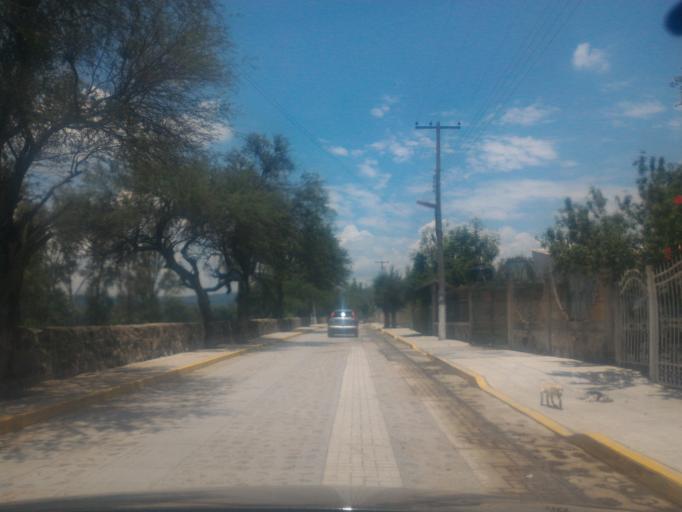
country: MX
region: Guanajuato
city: Ciudad Manuel Doblado
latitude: 20.7972
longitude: -101.9944
